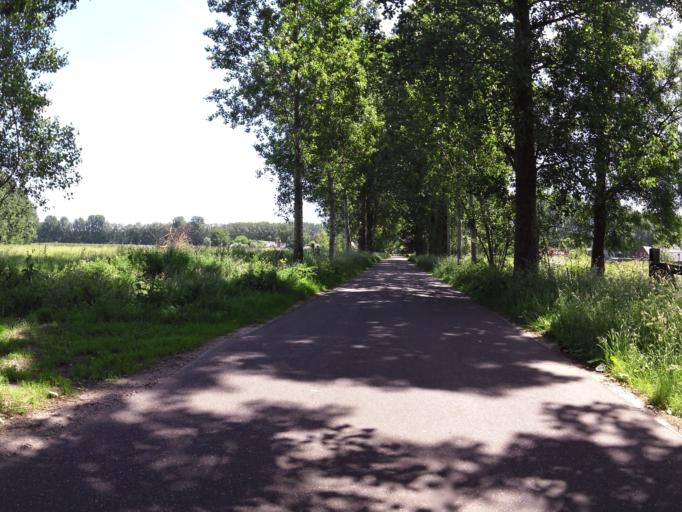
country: NL
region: North Brabant
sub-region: Gemeente Boxtel
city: Boxtel
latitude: 51.5910
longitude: 5.3643
